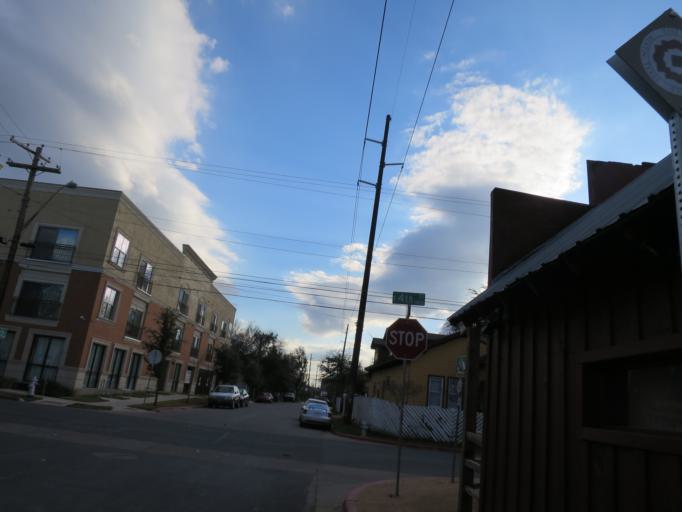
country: US
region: Texas
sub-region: Travis County
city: Austin
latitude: 30.2621
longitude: -97.7293
